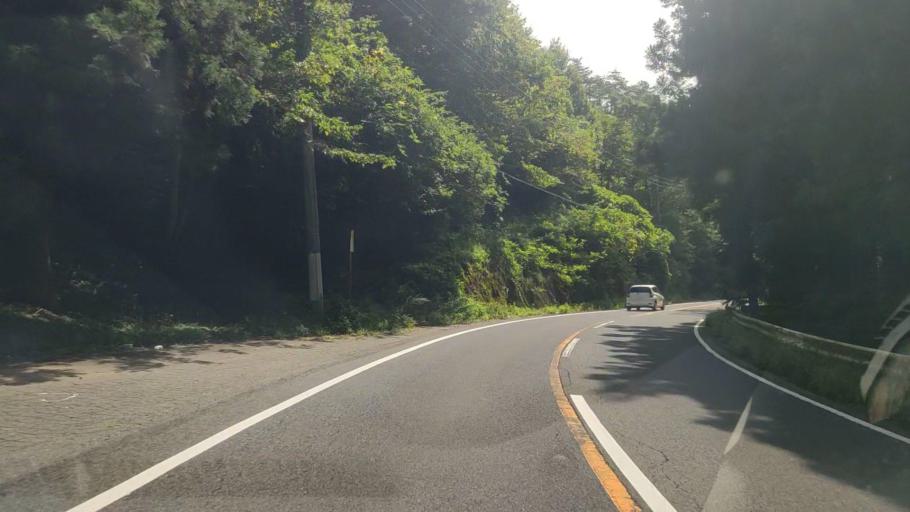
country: JP
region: Gunma
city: Numata
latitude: 36.6338
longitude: 138.9923
